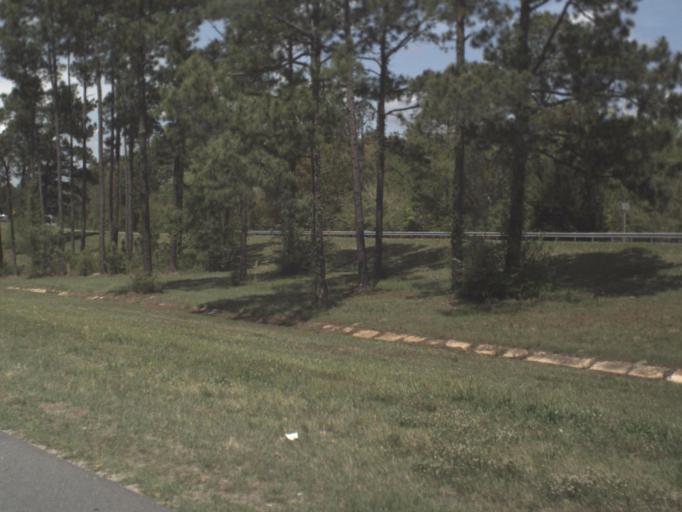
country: US
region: Florida
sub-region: Escambia County
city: Ensley
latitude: 30.5346
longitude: -87.3326
